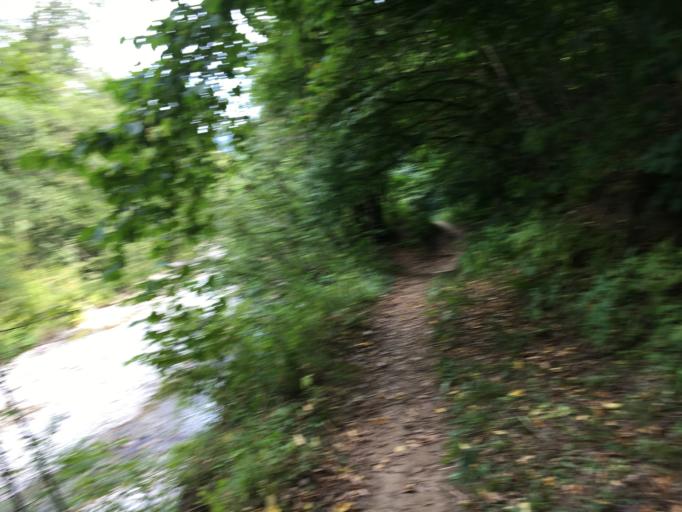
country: RU
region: Krasnodarskiy
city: Tuapse
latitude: 44.2556
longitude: 39.2250
